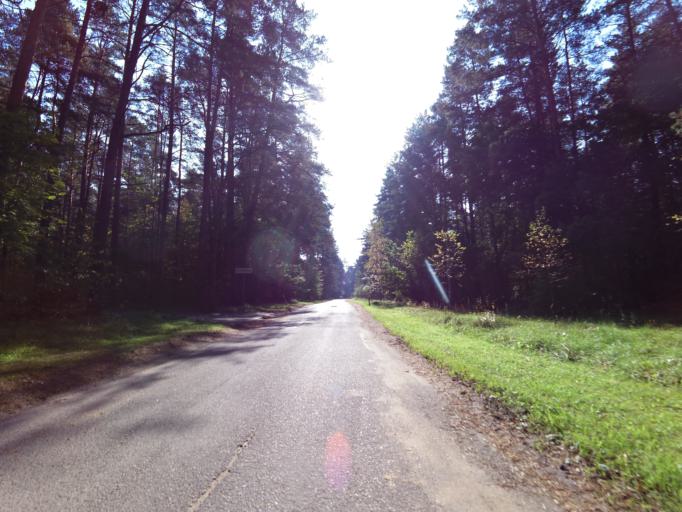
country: LT
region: Vilnius County
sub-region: Vilnius
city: Vilnius
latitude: 54.7383
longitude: 25.3058
